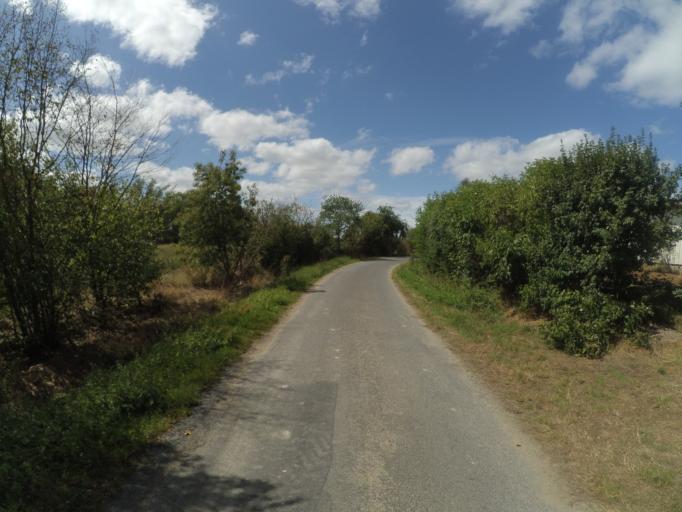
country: FR
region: Pays de la Loire
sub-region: Departement de la Loire-Atlantique
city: Saint-Hilaire-de-Clisson
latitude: 47.0403
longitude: -1.3309
